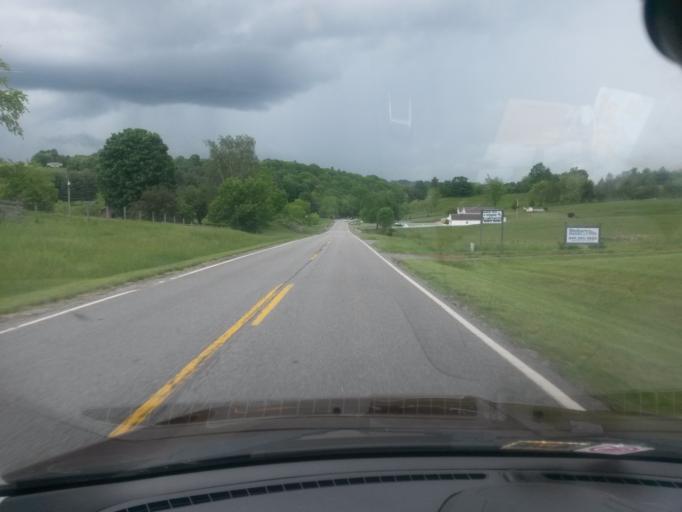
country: US
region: Virginia
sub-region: Floyd County
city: Floyd
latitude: 36.9529
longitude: -80.3628
